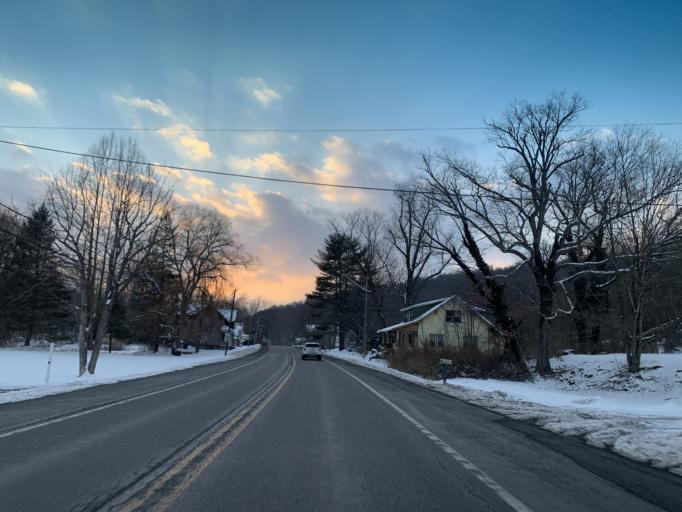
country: US
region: Maryland
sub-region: Allegany County
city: La Vale
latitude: 39.7008
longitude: -78.8452
